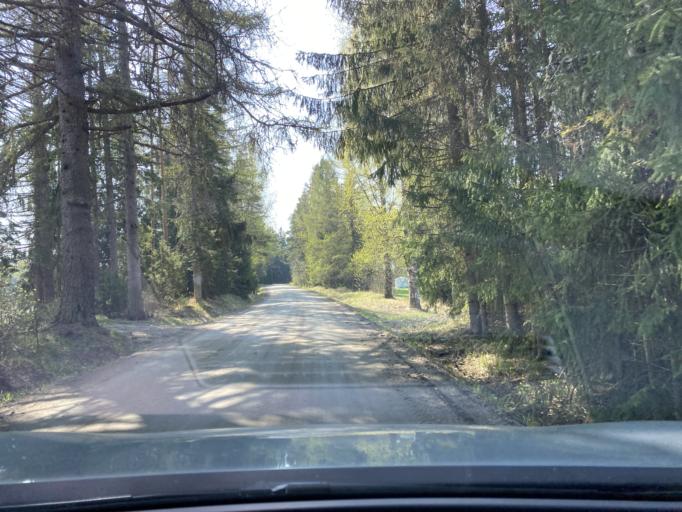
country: FI
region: Satakunta
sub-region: Pori
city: Huittinen
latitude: 61.1402
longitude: 22.8324
